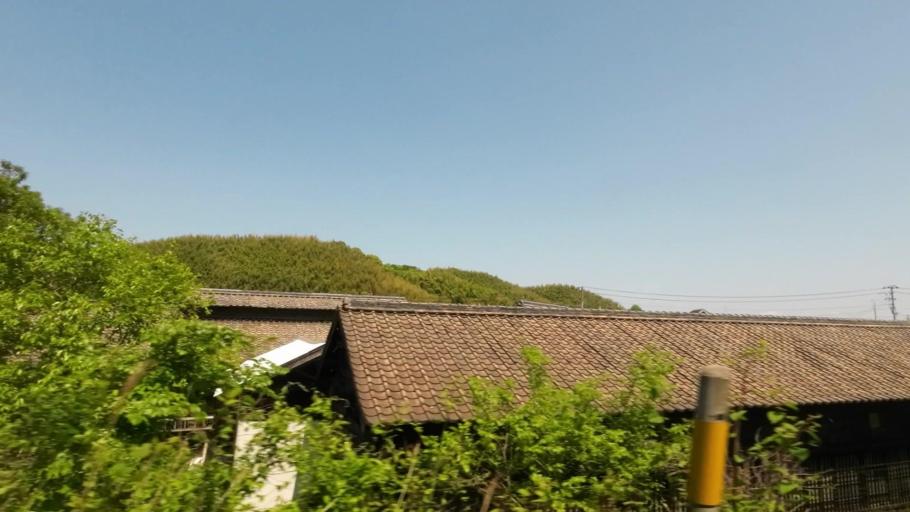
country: JP
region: Ehime
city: Hojo
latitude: 34.0622
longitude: 132.8995
